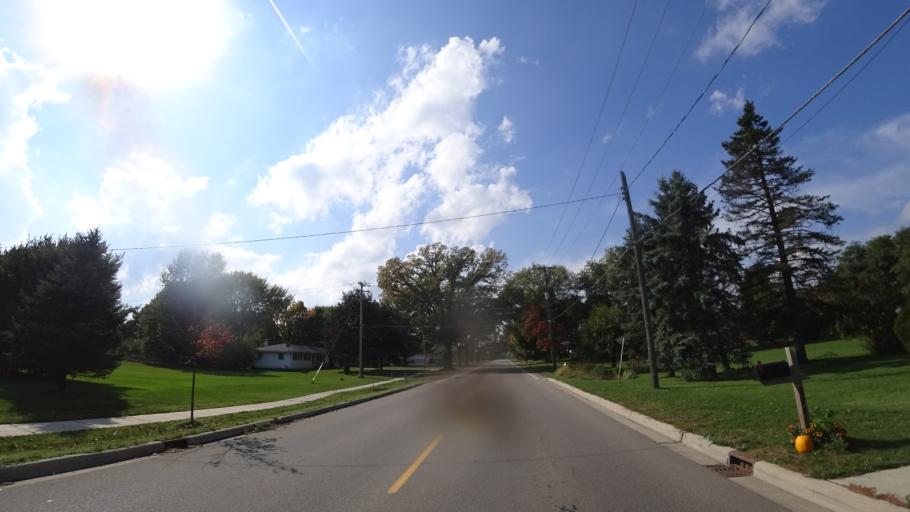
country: US
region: Michigan
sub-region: Saint Joseph County
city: Centreville
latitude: 42.0064
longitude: -85.4614
